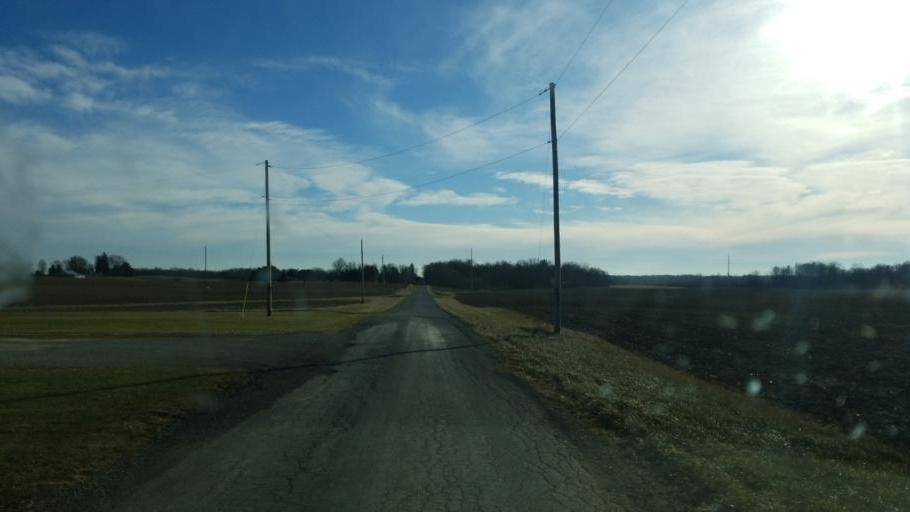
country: US
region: Ohio
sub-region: Richland County
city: Lexington
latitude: 40.6734
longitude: -82.6896
